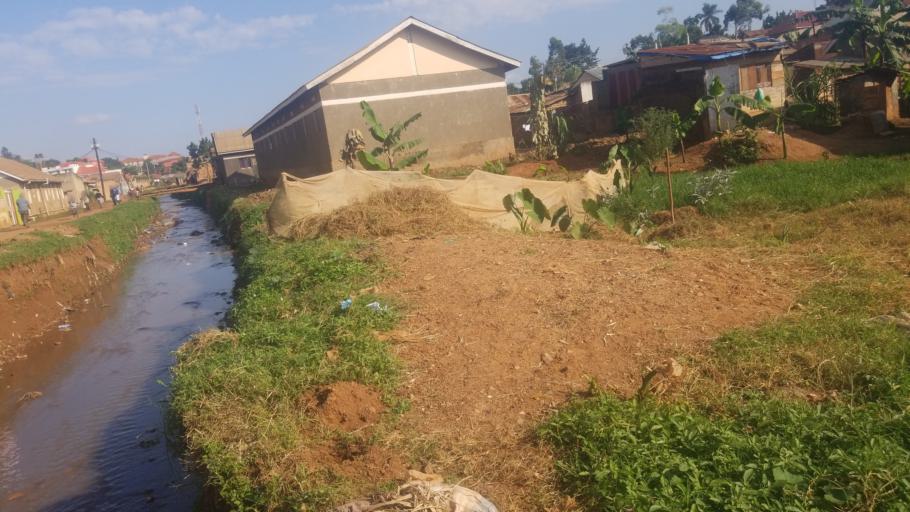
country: UG
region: Central Region
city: Kampala Central Division
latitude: 0.3439
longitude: 32.5572
